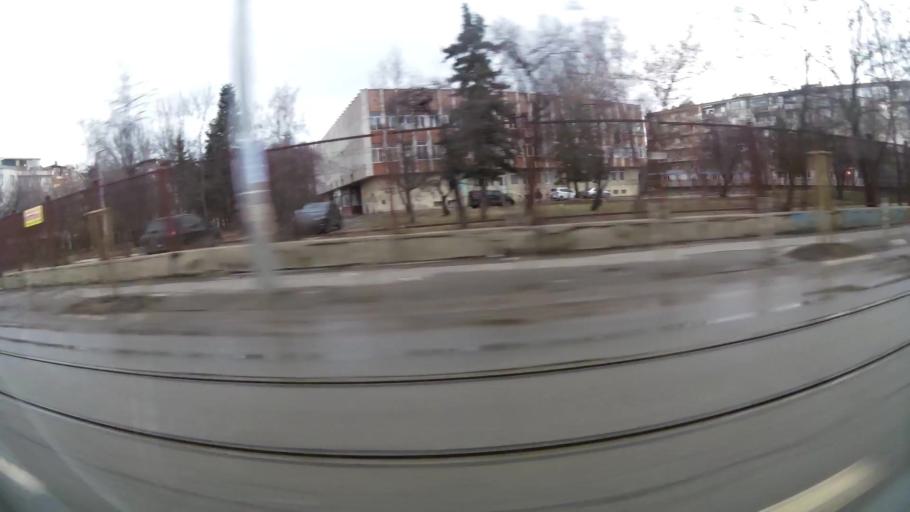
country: BG
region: Sofia-Capital
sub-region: Stolichna Obshtina
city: Sofia
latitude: 42.7367
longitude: 23.3026
